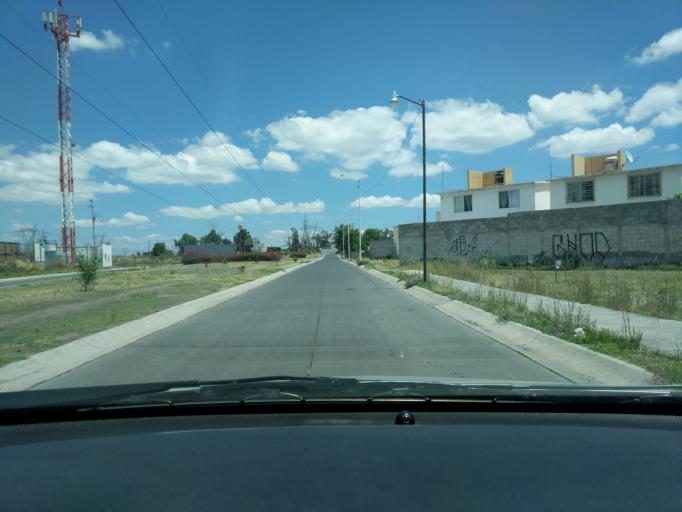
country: MX
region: Guanajuato
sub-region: Salamanca
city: El Divisador
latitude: 20.6013
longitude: -101.1745
